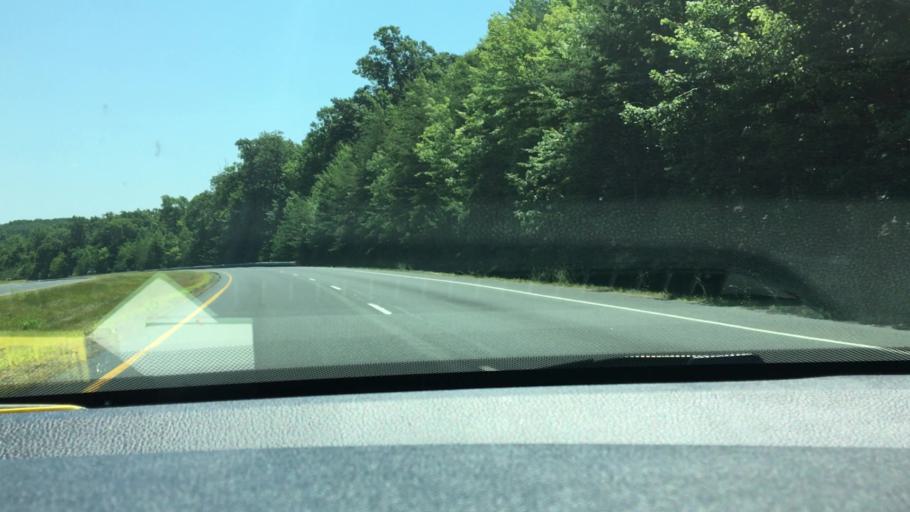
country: US
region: Virginia
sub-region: Prince William County
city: Buckhall
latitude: 38.6873
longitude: -77.3852
